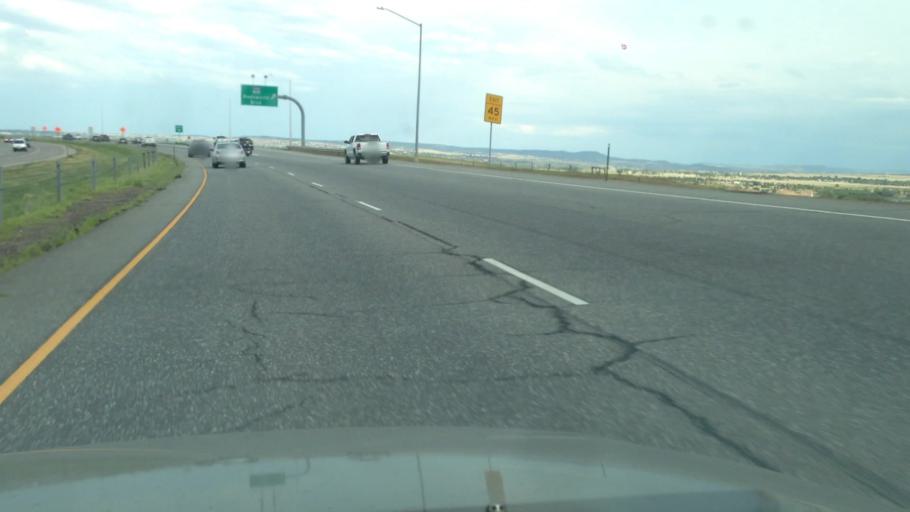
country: US
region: Colorado
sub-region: Jefferson County
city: Ken Caryl
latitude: 39.5540
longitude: -105.0923
